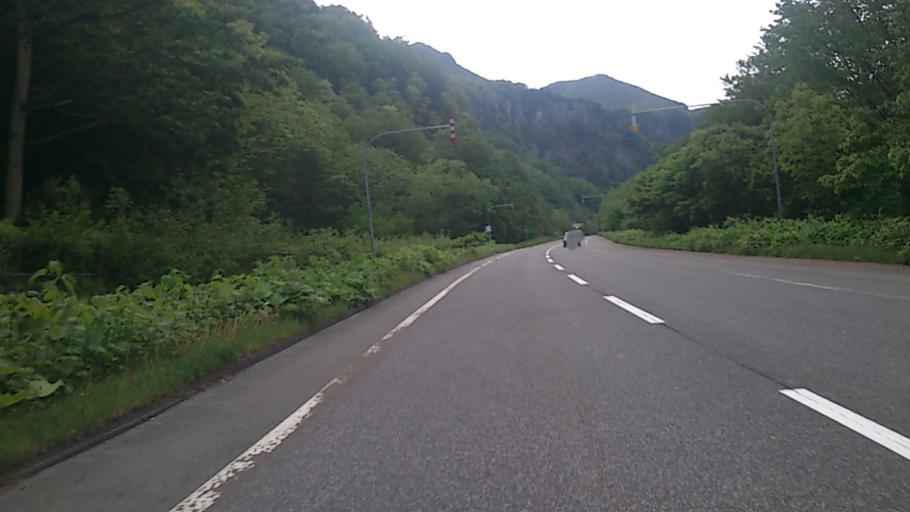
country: JP
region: Hokkaido
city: Kamikawa
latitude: 43.7565
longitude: 142.9254
